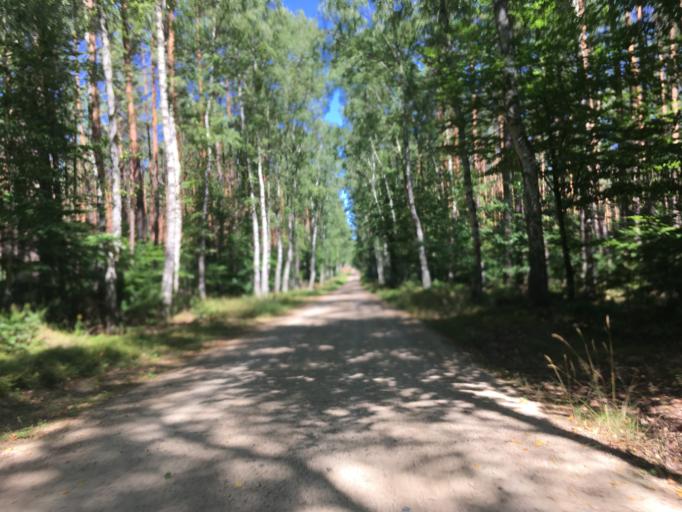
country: DE
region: Brandenburg
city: Rheinsberg
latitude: 53.1219
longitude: 12.9654
